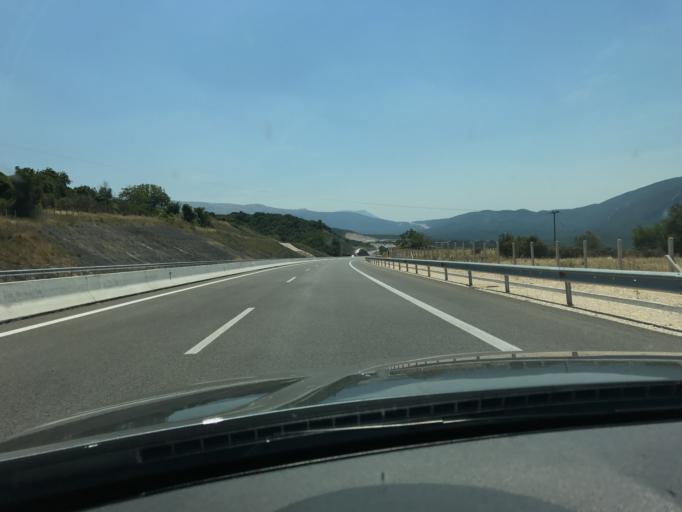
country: GR
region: Epirus
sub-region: Nomos Ioanninon
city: Agia Kyriaki
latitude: 39.4868
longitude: 20.8919
